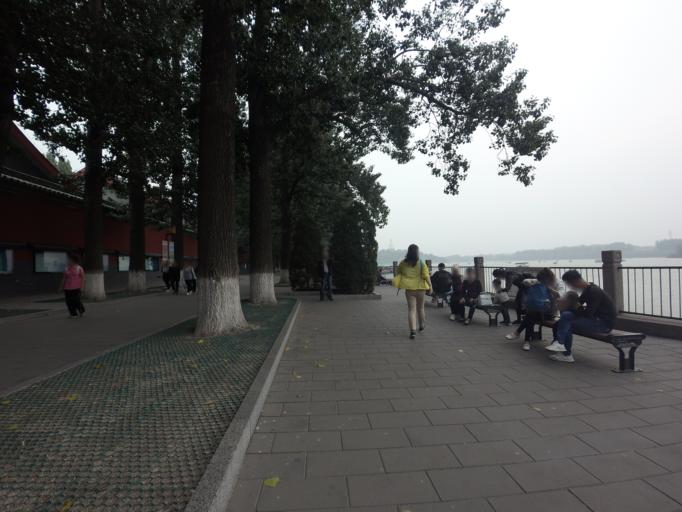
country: CN
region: Beijing
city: Jingshan
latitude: 39.9310
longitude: 116.3852
